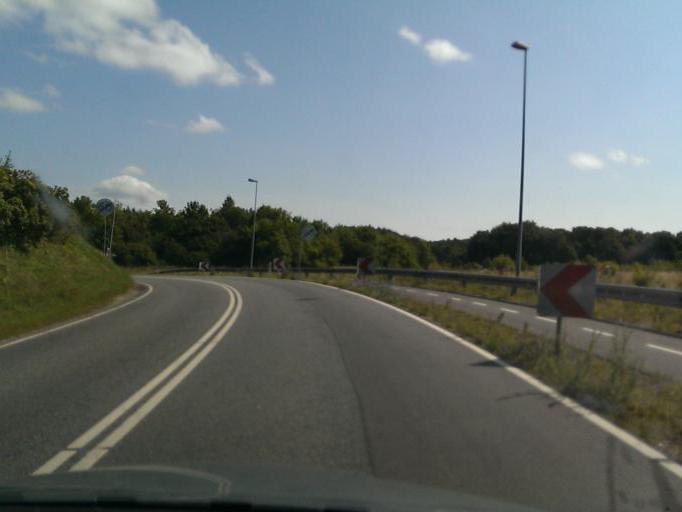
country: DK
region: Central Jutland
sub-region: Syddjurs Kommune
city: Ronde
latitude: 56.2396
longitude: 10.5678
